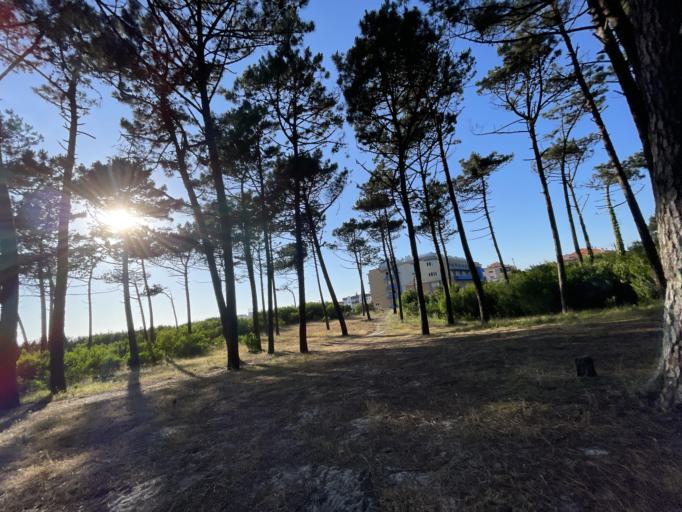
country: PT
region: Aveiro
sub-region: Ovar
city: Esmoriz
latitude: 40.9397
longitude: -8.6548
